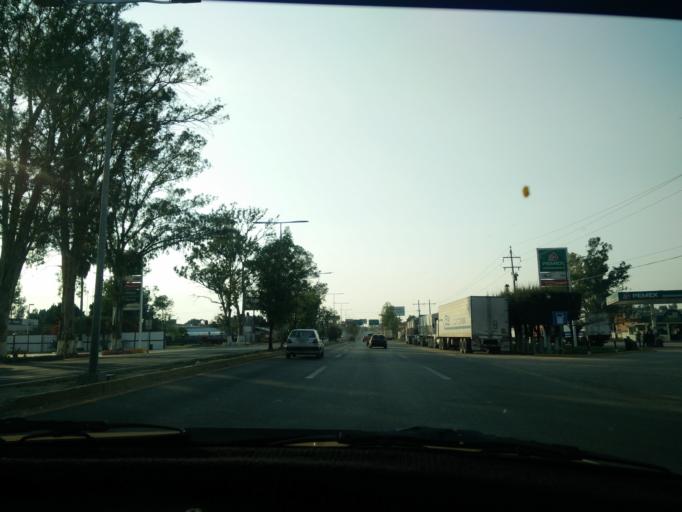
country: MX
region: Oaxaca
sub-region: Santa Maria Atzompa
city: Fraccionamiento Riberas de San Jeronimo
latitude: 17.1286
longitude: -96.7692
